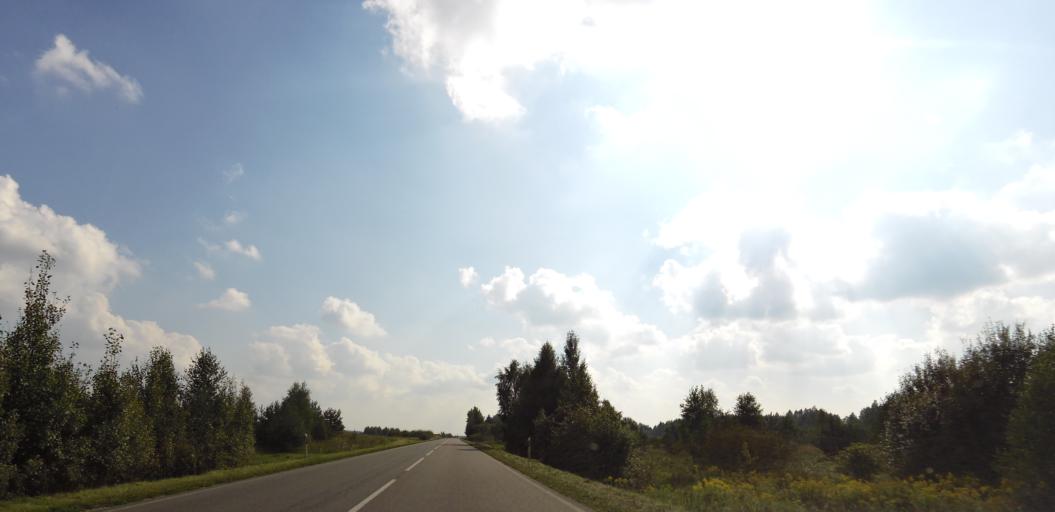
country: LT
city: Grigiskes
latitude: 54.7605
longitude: 25.0810
